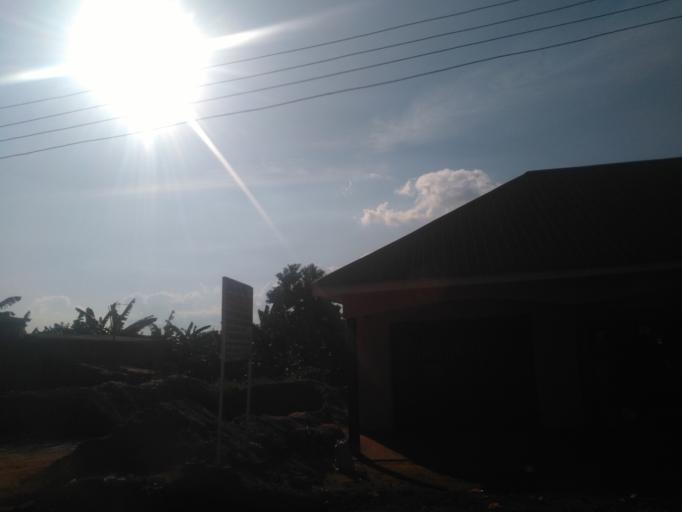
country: UG
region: Central Region
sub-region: Wakiso District
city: Kajansi
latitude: 0.2671
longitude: 32.4719
